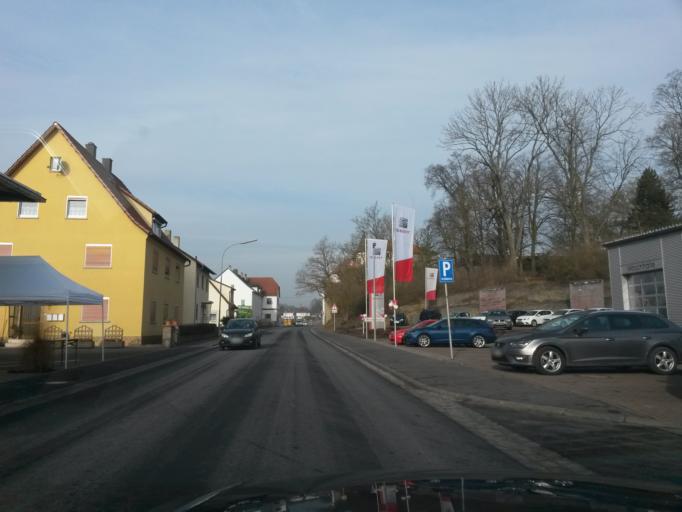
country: DE
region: Bavaria
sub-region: Regierungsbezirk Unterfranken
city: Ostheim vor der Rhon
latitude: 50.4594
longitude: 10.2230
